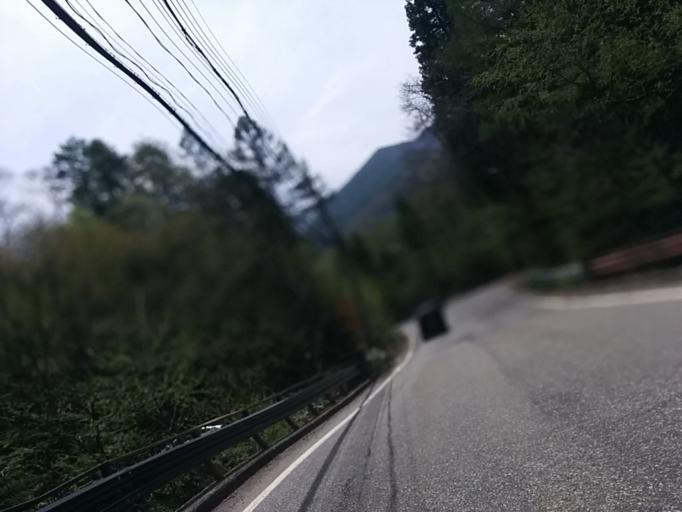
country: JP
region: Gifu
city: Takayama
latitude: 36.2222
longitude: 137.5418
